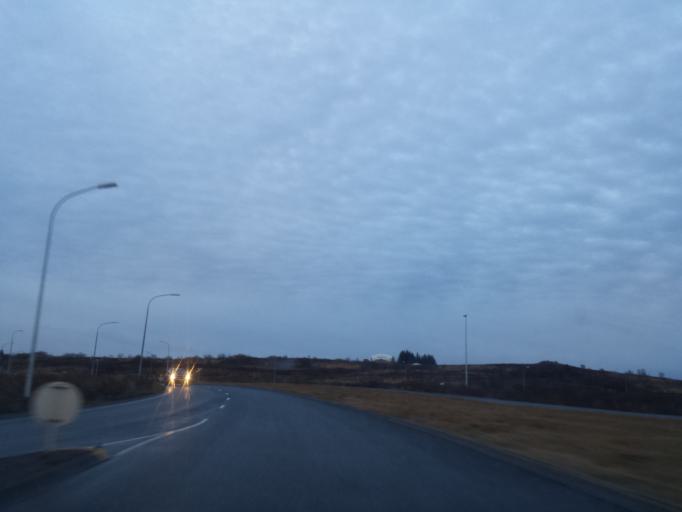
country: IS
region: Capital Region
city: Mosfellsbaer
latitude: 64.1388
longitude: -21.7572
